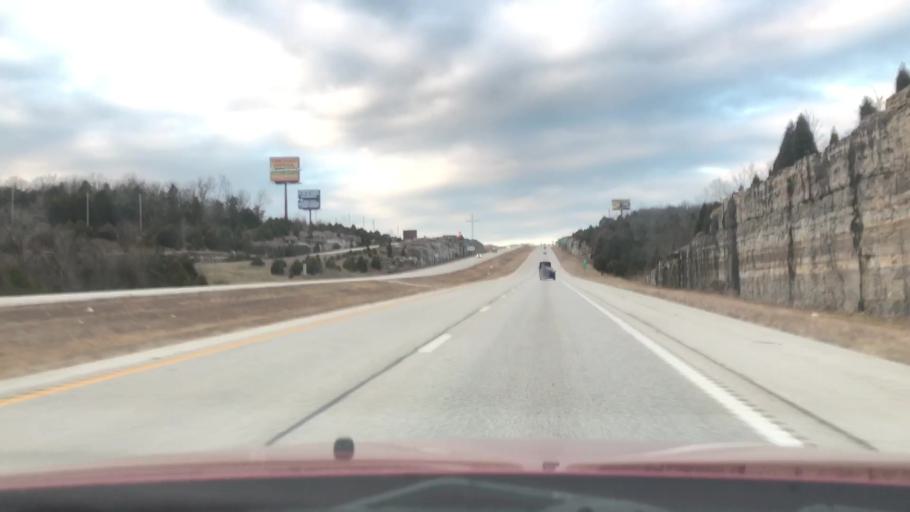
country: US
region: Missouri
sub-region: Taney County
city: Merriam Woods
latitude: 36.7376
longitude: -93.2213
